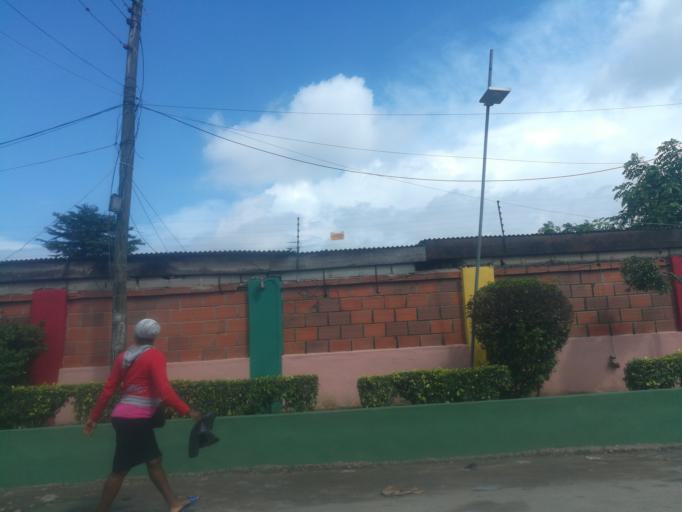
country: NG
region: Lagos
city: Somolu
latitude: 6.5468
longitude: 3.3777
